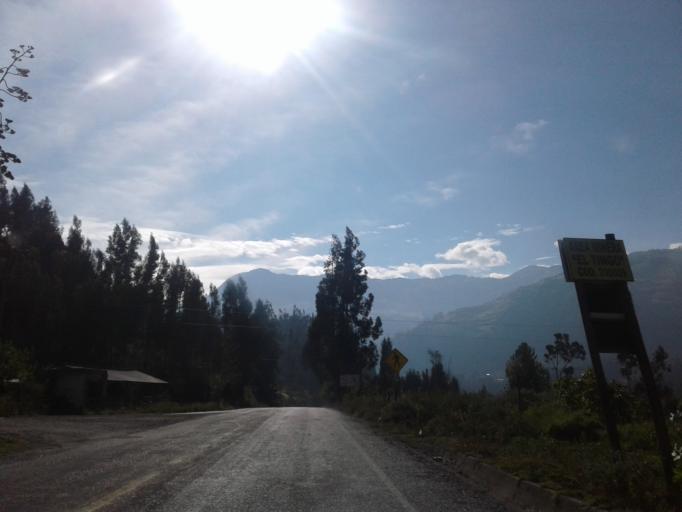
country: EC
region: Chimborazo
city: Guano
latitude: -1.5166
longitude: -78.5157
